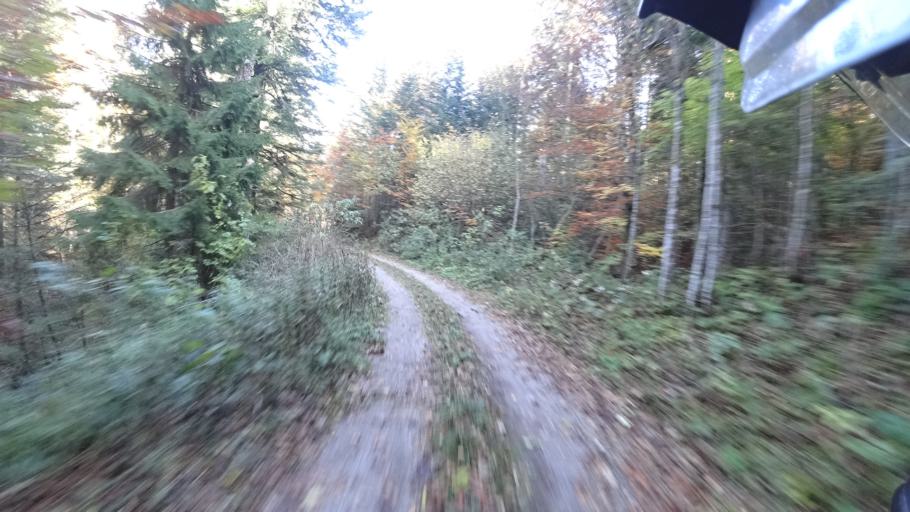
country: HR
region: Karlovacka
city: Plaski
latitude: 45.0383
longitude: 15.3428
